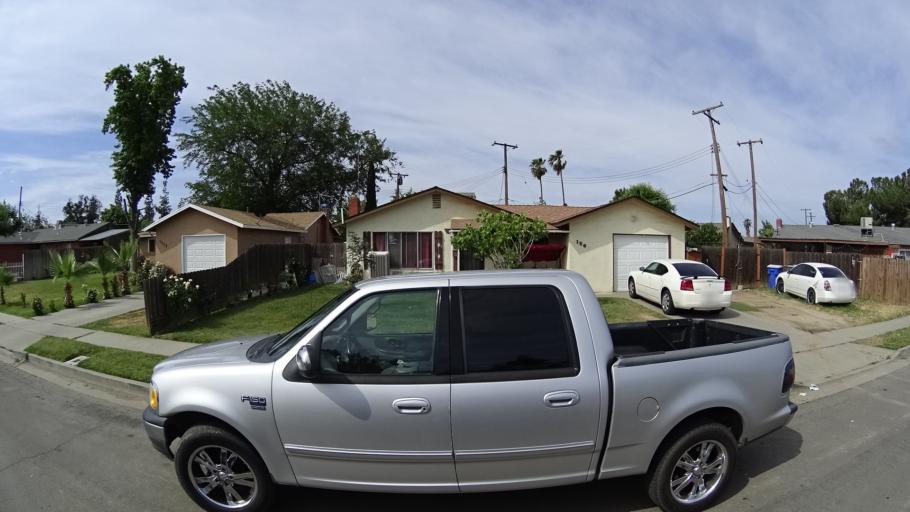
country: US
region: California
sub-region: Kings County
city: Hanford
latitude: 36.3148
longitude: -119.6696
